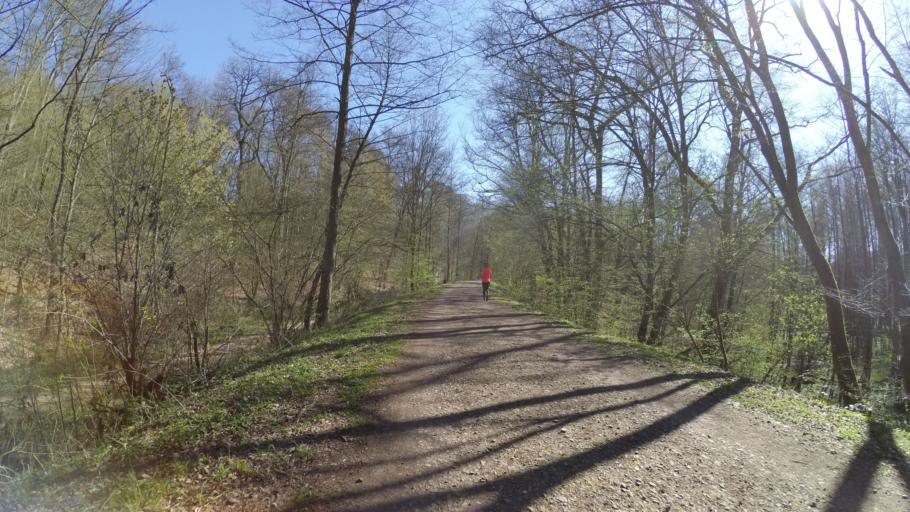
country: DE
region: Saarland
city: Puttlingen
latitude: 49.2634
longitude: 6.8793
